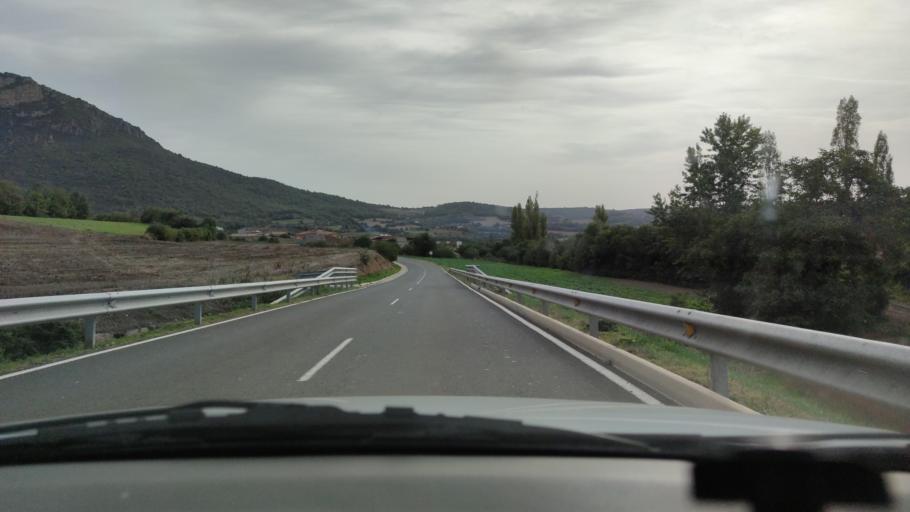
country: ES
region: Catalonia
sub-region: Provincia de Lleida
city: Artesa de Segre
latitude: 41.9933
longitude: 1.0142
